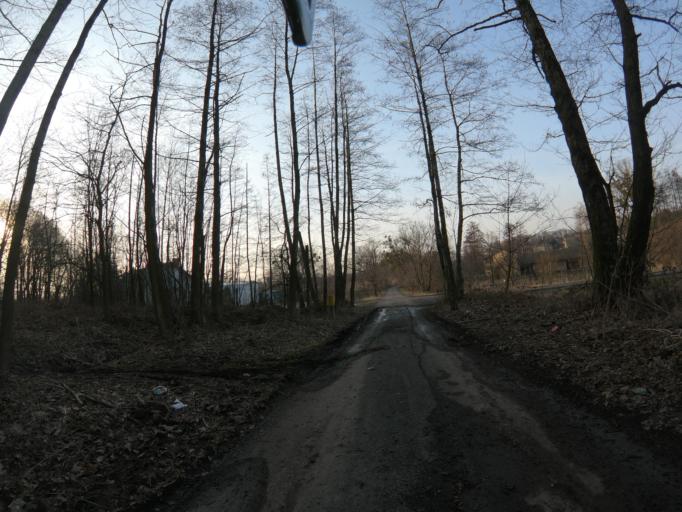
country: PL
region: Silesian Voivodeship
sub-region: Powiat raciborski
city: Pogrzebien
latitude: 50.0844
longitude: 18.2619
